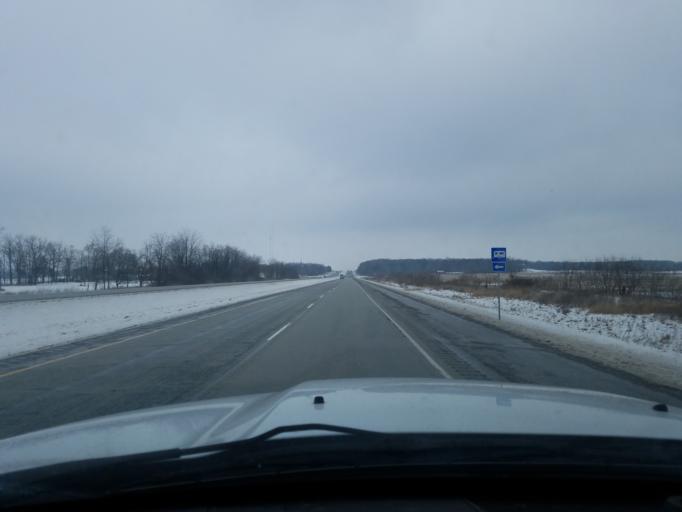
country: US
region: Indiana
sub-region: Fulton County
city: Rochester
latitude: 41.1034
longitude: -86.2397
